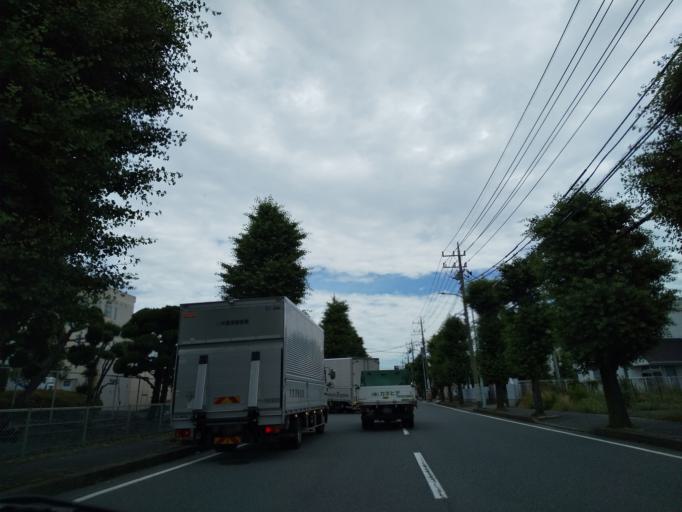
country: JP
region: Kanagawa
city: Zama
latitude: 35.5170
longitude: 139.3557
